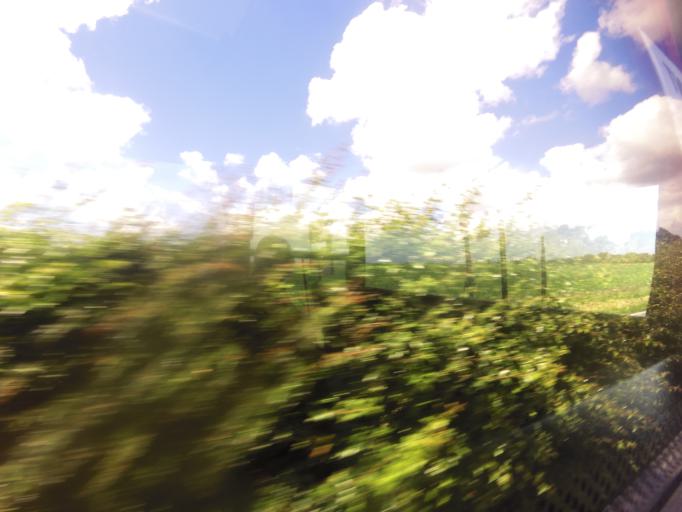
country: GB
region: England
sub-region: Norfolk
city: Aylsham
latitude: 52.8373
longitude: 1.2716
